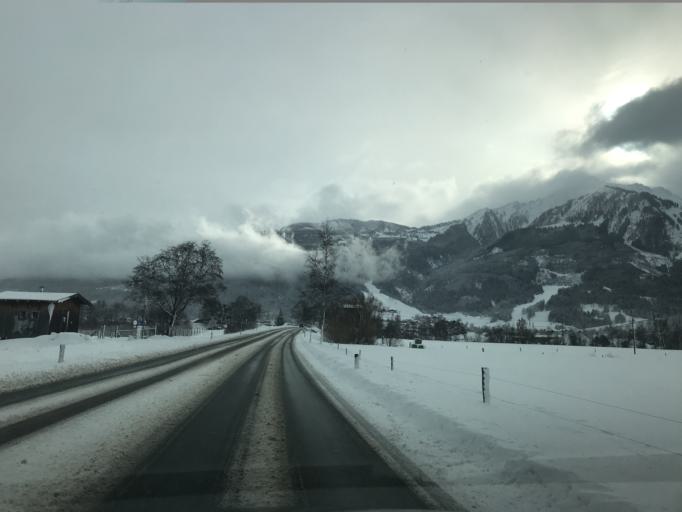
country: AT
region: Salzburg
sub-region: Politischer Bezirk Zell am See
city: Kaprun
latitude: 47.2861
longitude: 12.7495
